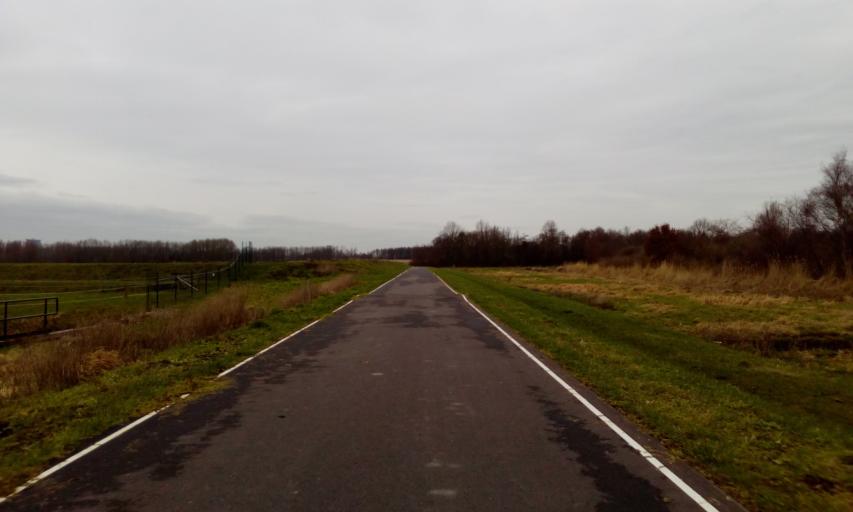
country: NL
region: South Holland
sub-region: Gemeente Pijnacker-Nootdorp
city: Pijnacker
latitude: 51.9814
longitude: 4.4067
